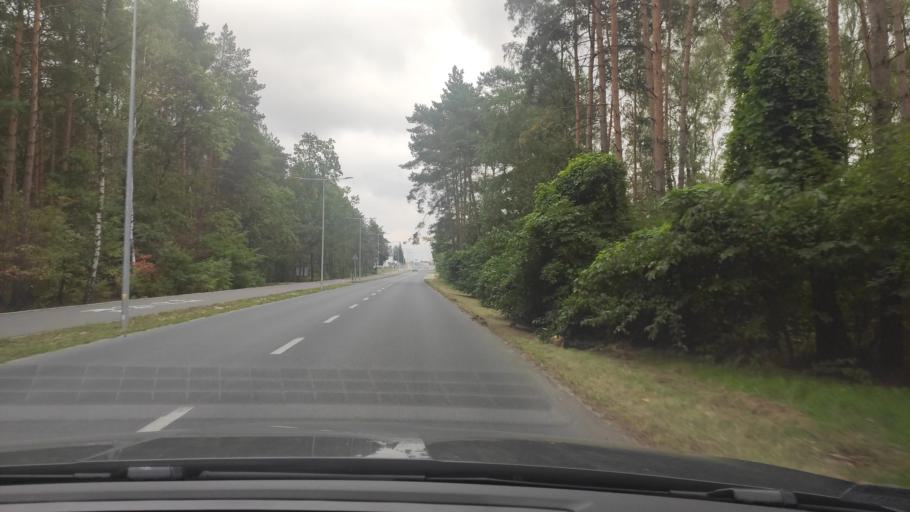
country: PL
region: Greater Poland Voivodeship
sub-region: Powiat poznanski
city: Swarzedz
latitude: 52.3856
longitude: 17.0553
